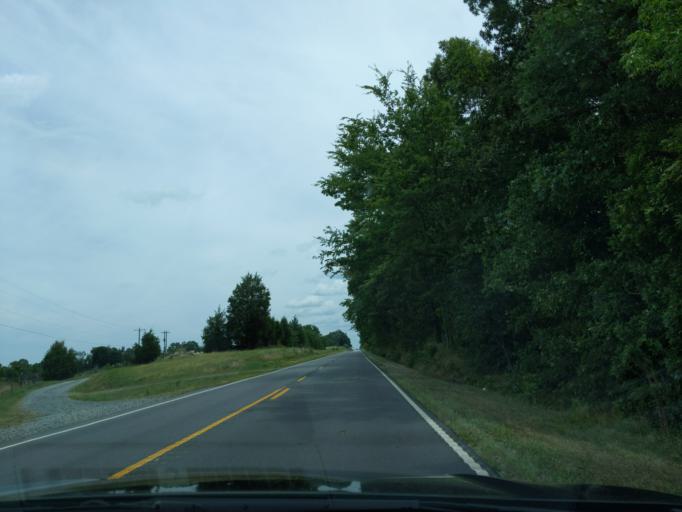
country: US
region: North Carolina
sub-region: Cabarrus County
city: Mount Pleasant
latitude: 35.4451
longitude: -80.3579
